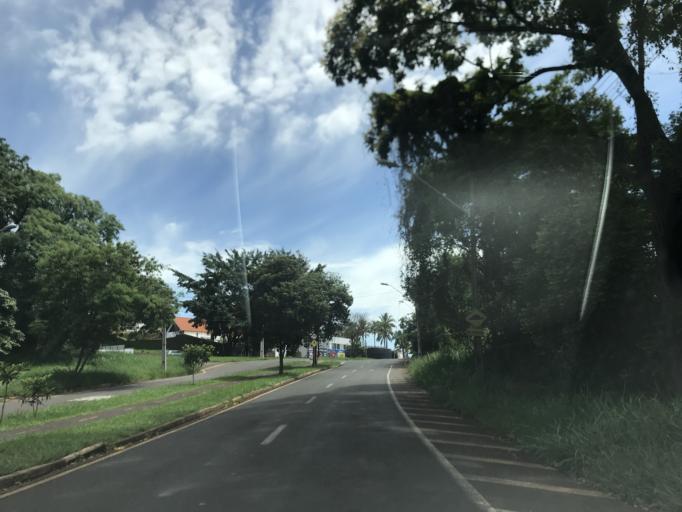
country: BR
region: Parana
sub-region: Londrina
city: Londrina
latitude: -23.3398
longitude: -51.1642
